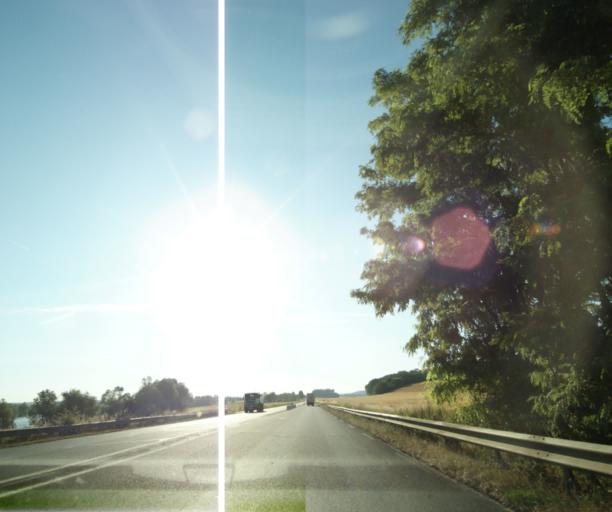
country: FR
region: Ile-de-France
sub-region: Departement de Seine-et-Marne
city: La Grande-Paroisse
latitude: 48.3613
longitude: 2.8749
